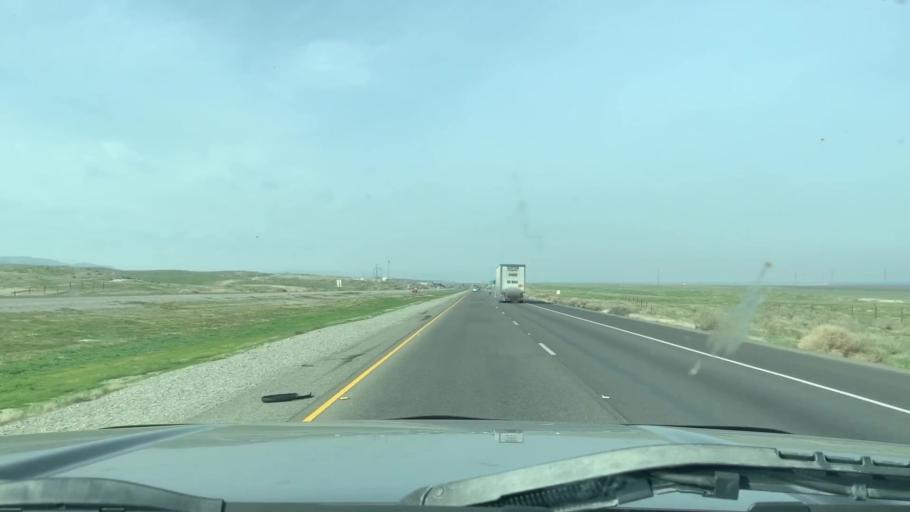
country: US
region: California
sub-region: Fresno County
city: Mendota
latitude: 36.5247
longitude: -120.4796
